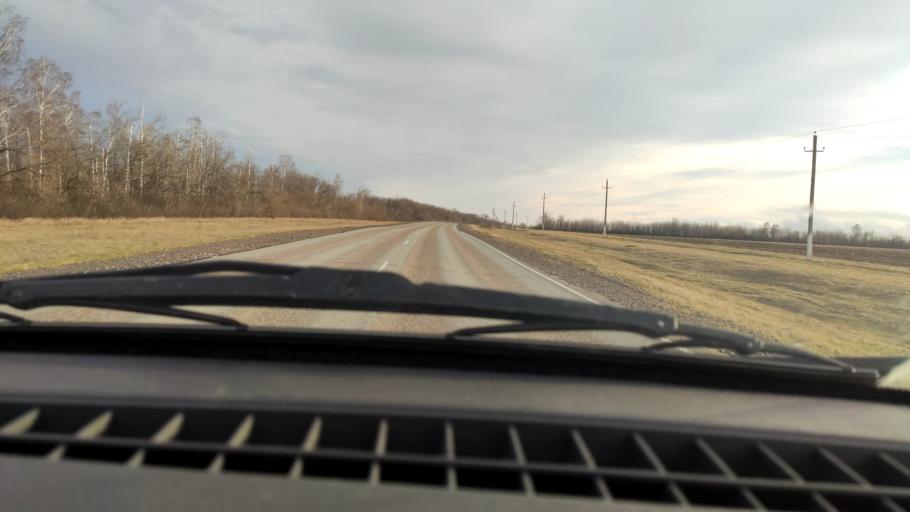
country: RU
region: Bashkortostan
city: Davlekanovo
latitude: 54.3311
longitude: 55.1664
